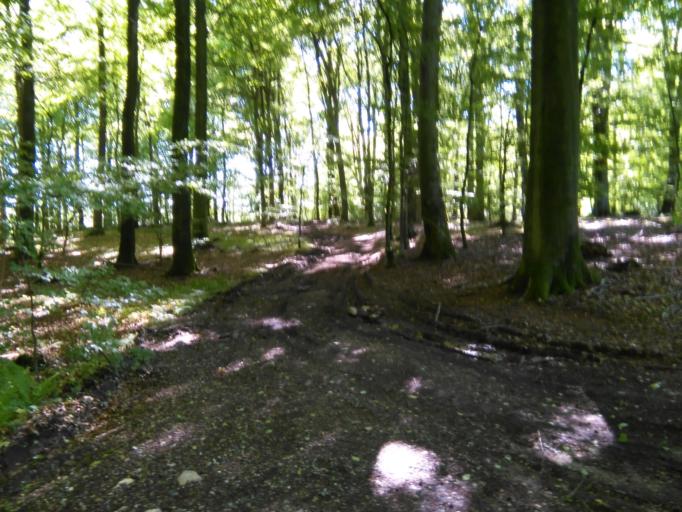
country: DK
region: Central Jutland
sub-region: Arhus Kommune
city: Malling
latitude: 56.0231
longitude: 10.1633
